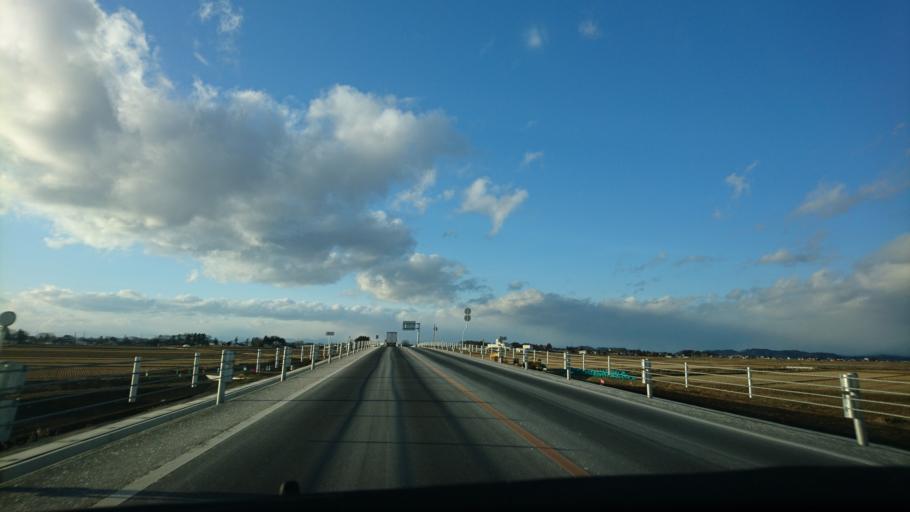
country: JP
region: Miyagi
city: Wakuya
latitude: 38.6795
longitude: 141.2572
